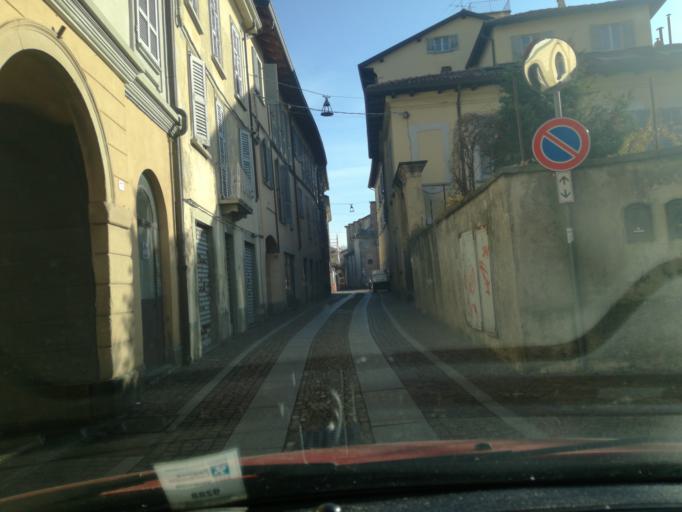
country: IT
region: Lombardy
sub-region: Provincia di Lecco
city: Merate
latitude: 45.6977
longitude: 9.4203
